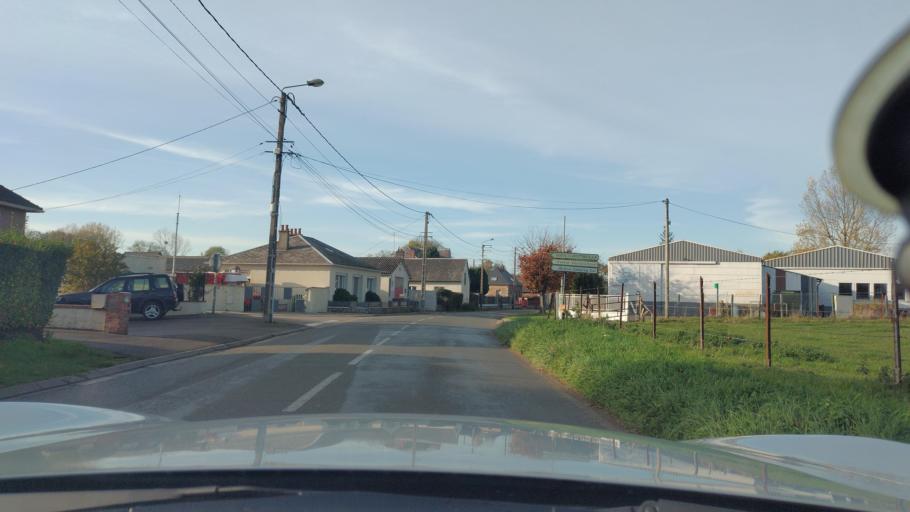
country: FR
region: Picardie
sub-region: Departement de la Somme
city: Friville-Escarbotin
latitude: 50.1036
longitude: 1.5309
